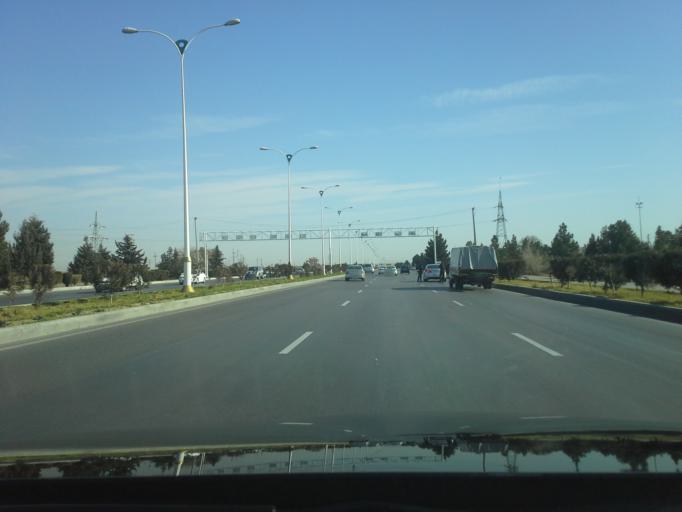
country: TM
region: Ahal
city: Annau
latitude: 37.9170
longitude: 58.4658
